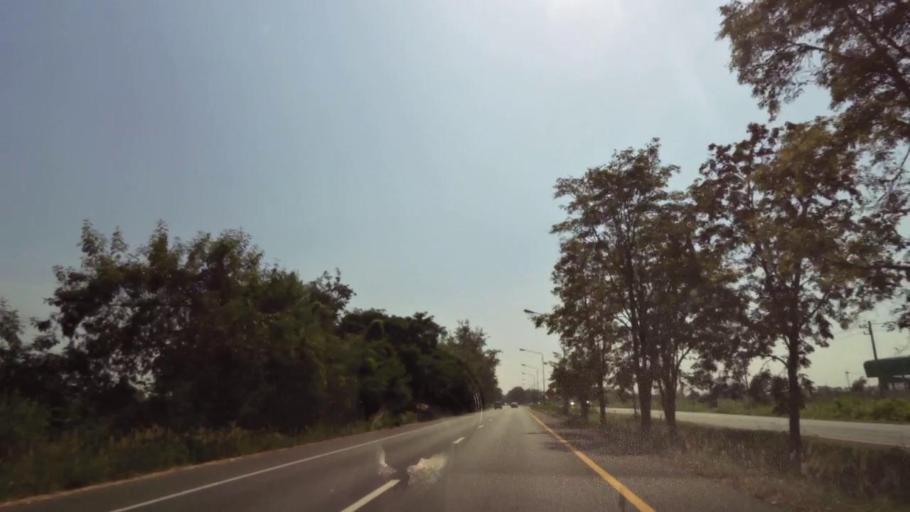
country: TH
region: Nakhon Sawan
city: Kao Liao
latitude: 15.9321
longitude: 100.1126
